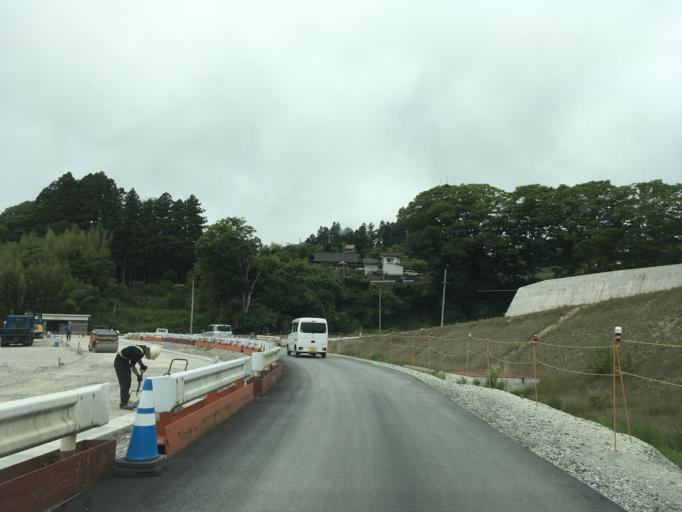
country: JP
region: Iwate
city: Ofunato
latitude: 38.8908
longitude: 141.6411
